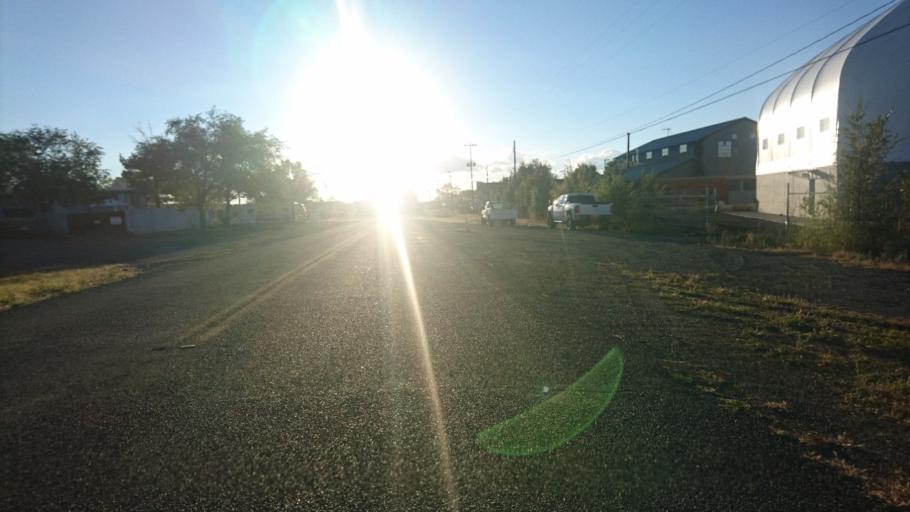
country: US
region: Arizona
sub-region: Coconino County
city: Williams
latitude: 35.2227
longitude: -112.4910
